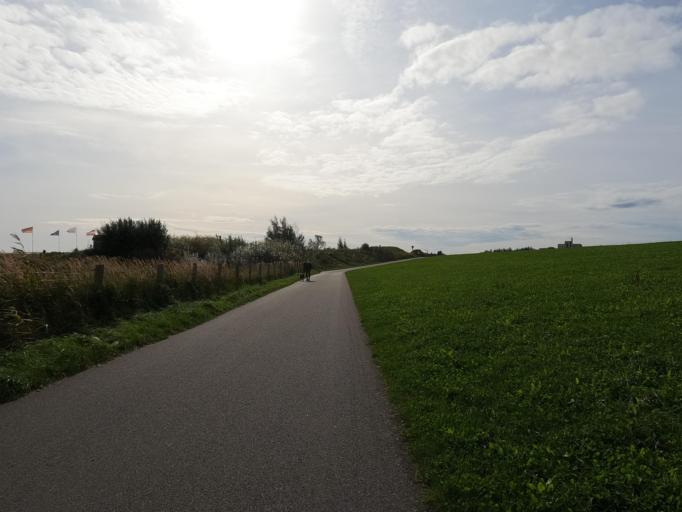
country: DE
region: Schleswig-Holstein
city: Dahme
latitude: 54.2323
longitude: 11.0845
